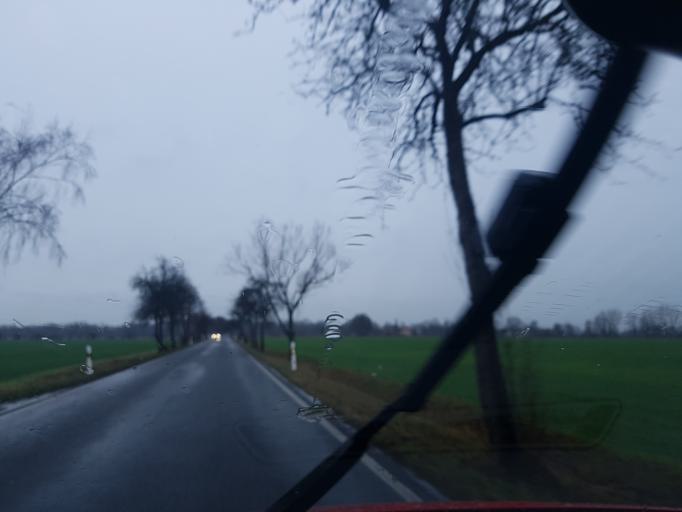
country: DE
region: Brandenburg
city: Schilda
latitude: 51.6137
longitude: 13.3187
